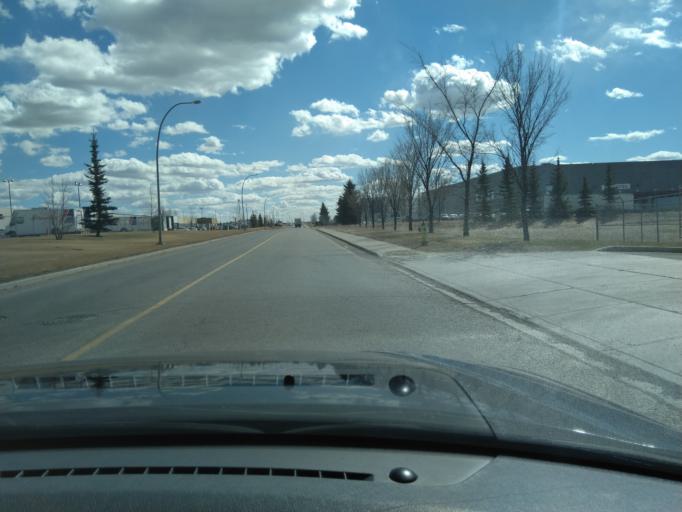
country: CA
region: Alberta
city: Calgary
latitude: 51.1204
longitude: -114.0349
